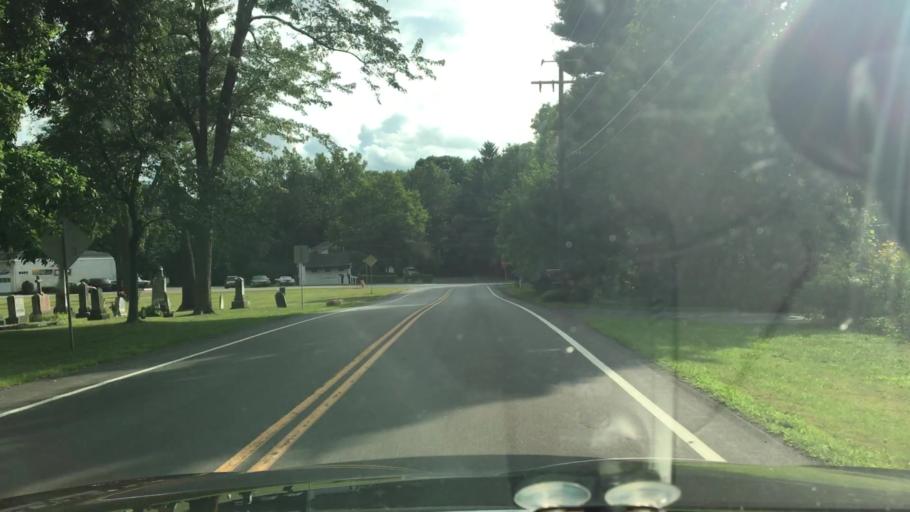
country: US
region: New York
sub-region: Erie County
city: Elma Center
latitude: 42.8176
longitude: -78.6729
